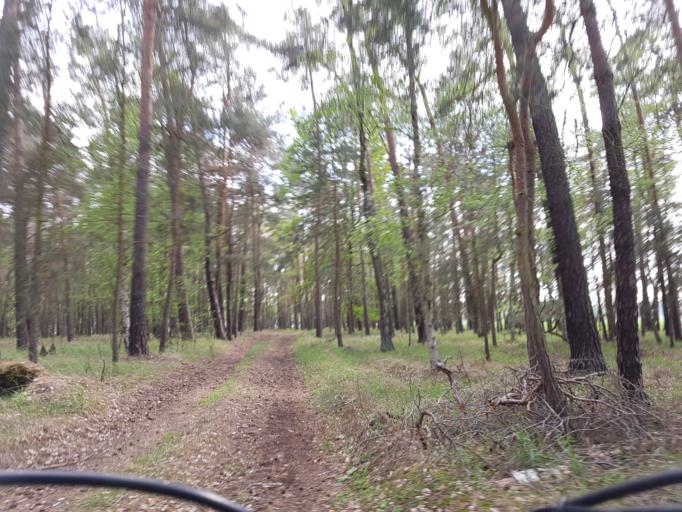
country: DE
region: Brandenburg
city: Schilda
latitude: 51.5957
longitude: 13.3708
